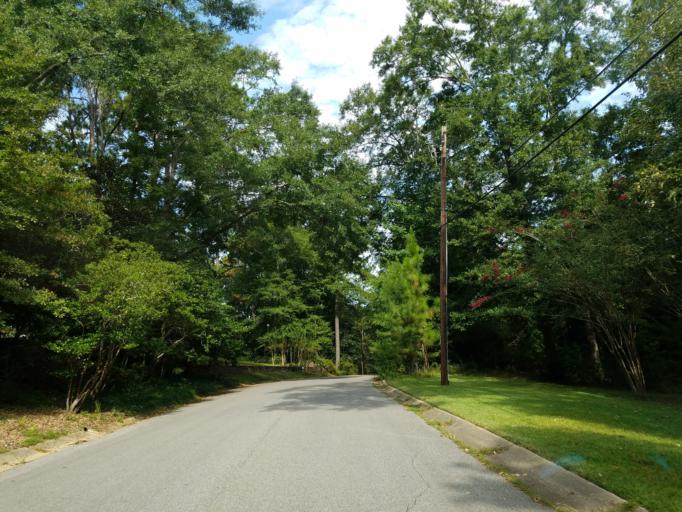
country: US
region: Mississippi
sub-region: Lamar County
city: West Hattiesburg
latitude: 31.3163
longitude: -89.3434
